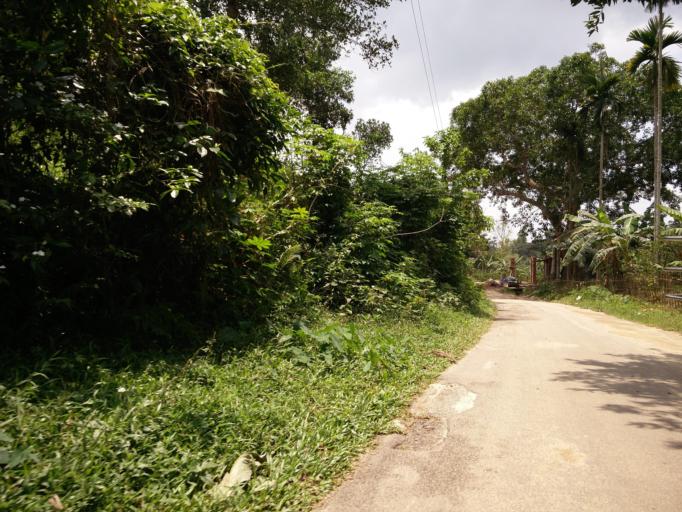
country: IN
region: Tripura
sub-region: Dhalai
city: Kamalpur
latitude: 24.3042
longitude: 91.7781
